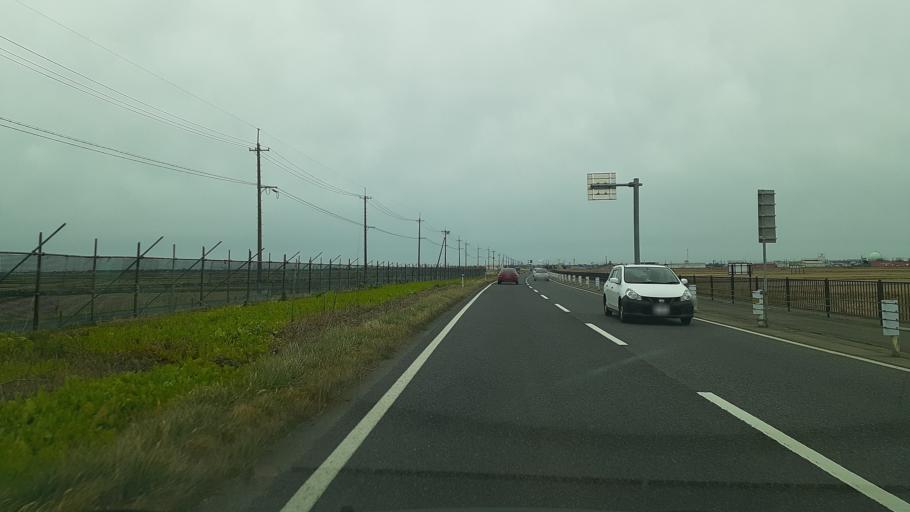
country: JP
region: Niigata
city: Niitsu-honcho
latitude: 37.8048
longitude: 139.1020
